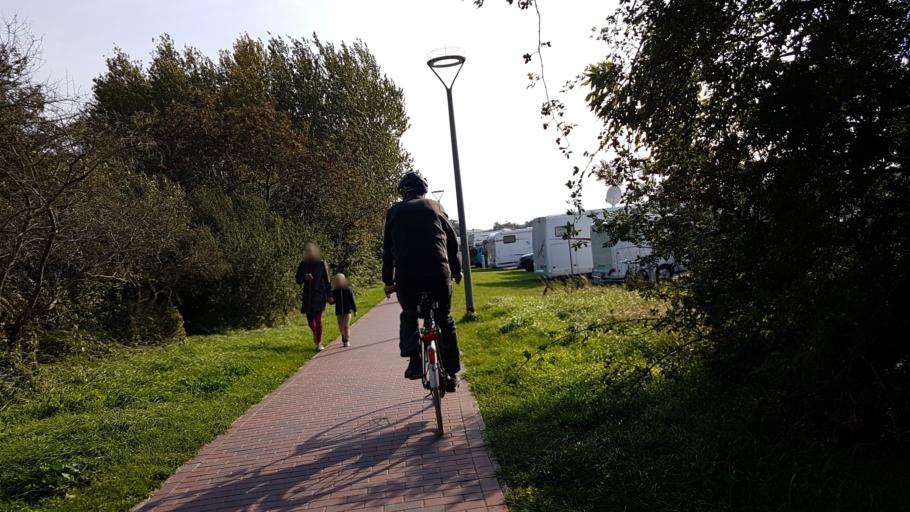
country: DE
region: Mecklenburg-Vorpommern
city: Glowe
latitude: 54.5744
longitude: 13.4704
